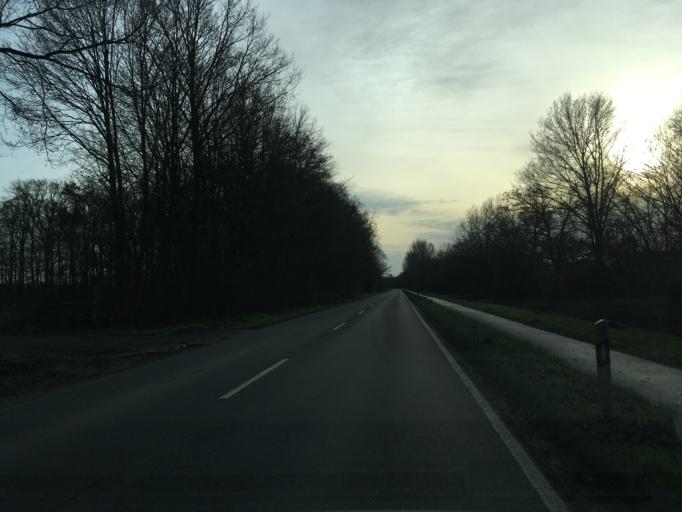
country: DE
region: North Rhine-Westphalia
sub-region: Regierungsbezirk Munster
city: Ahaus
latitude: 52.0627
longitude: 7.0148
